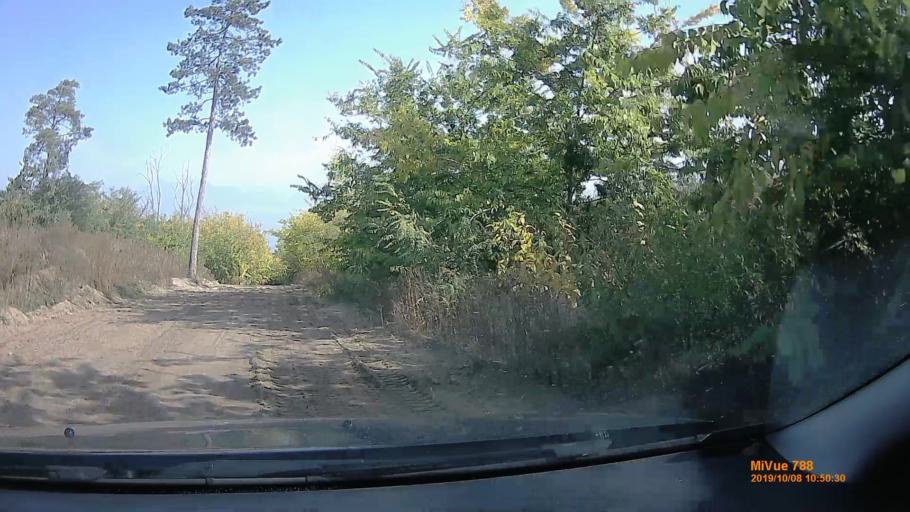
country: HU
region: Pest
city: Dunakeszi
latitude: 47.6606
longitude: 19.1565
